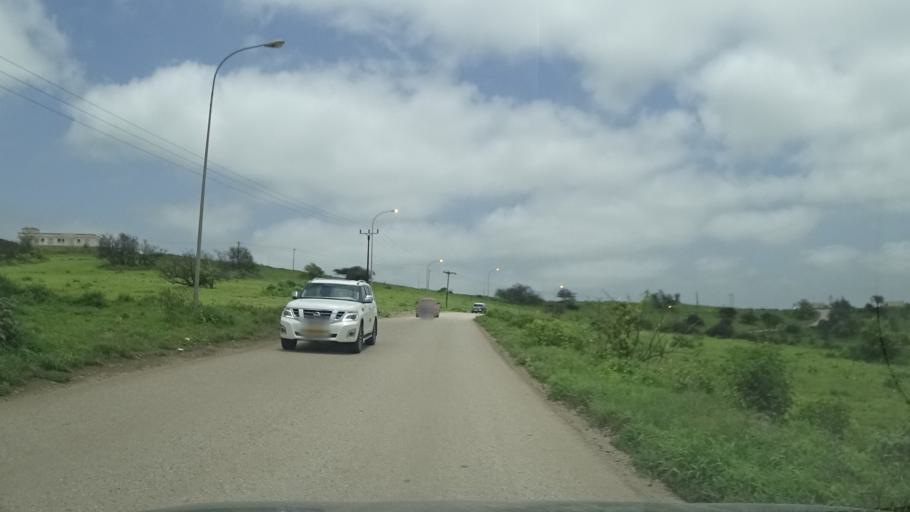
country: OM
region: Zufar
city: Salalah
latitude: 17.1894
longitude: 54.1618
